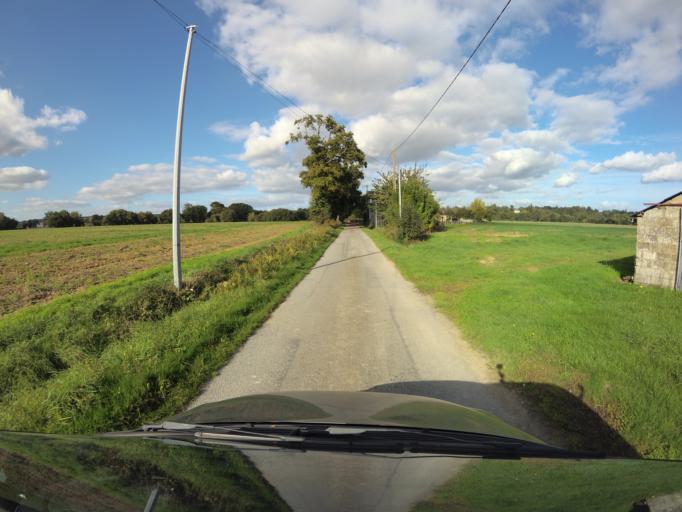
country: FR
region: Brittany
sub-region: Departement du Morbihan
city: Saint-Martin-sur-Oust
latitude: 47.7359
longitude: -2.2416
